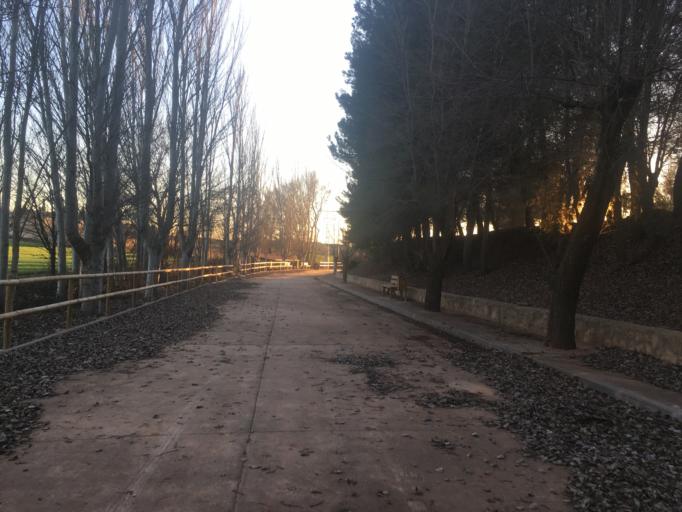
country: ES
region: Castille-La Mancha
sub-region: Provincia de Cuenca
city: Atalaya del Canavate
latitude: 39.5536
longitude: -2.2520
